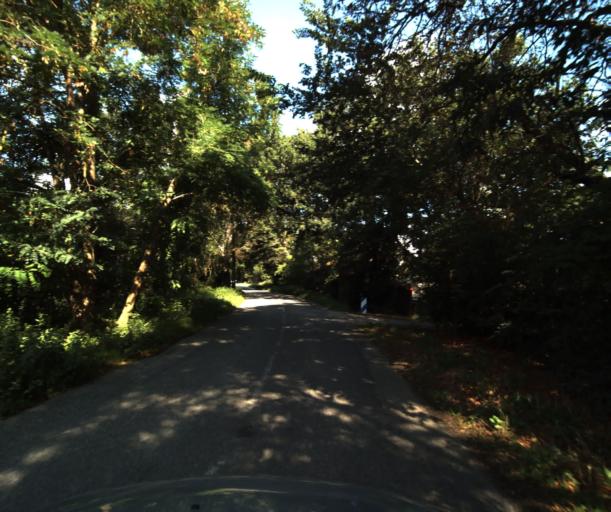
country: FR
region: Midi-Pyrenees
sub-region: Departement de la Haute-Garonne
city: Portet-sur-Garonne
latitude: 43.5152
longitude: 1.4197
